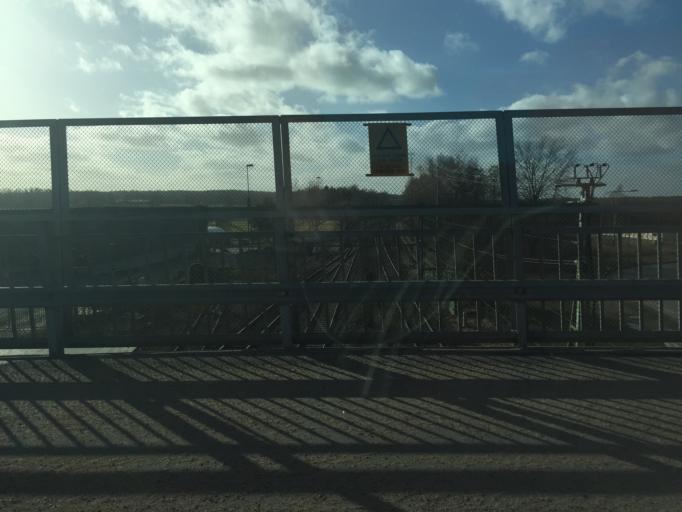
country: SE
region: Soedermanland
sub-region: Vingakers Kommun
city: Vingaker
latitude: 59.0417
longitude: 15.8714
